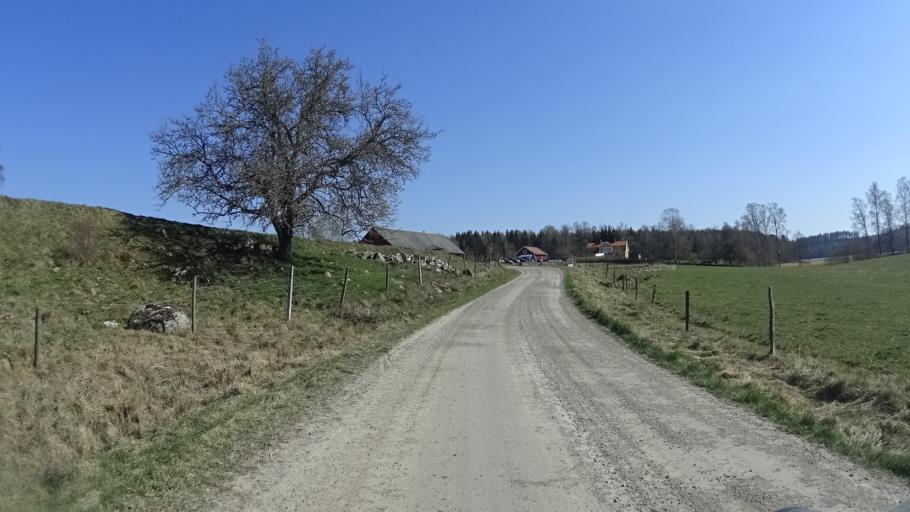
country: SE
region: OEstergoetland
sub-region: Kinda Kommun
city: Rimforsa
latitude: 58.2565
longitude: 15.5862
